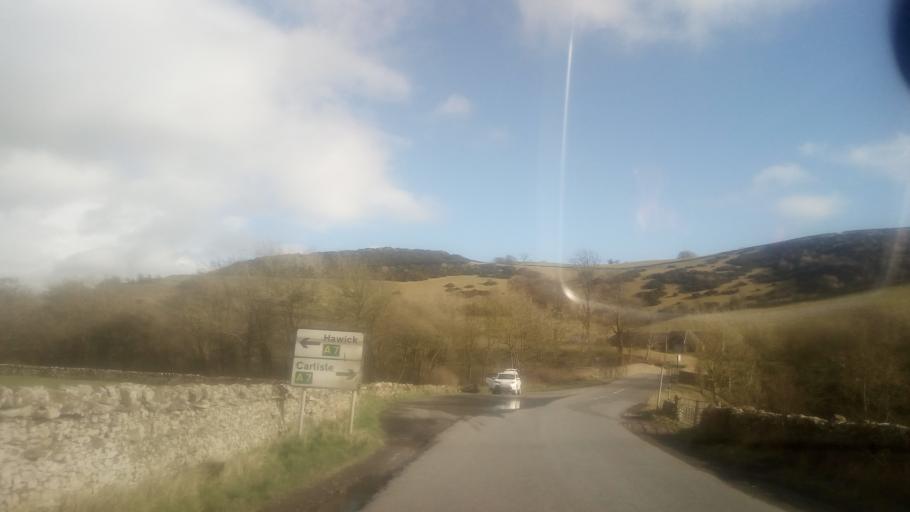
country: GB
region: Scotland
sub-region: The Scottish Borders
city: Hawick
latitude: 55.4127
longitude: -2.8218
